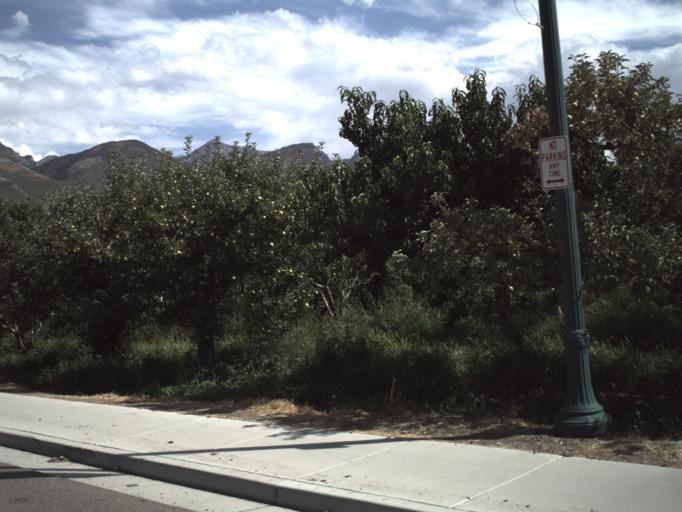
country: US
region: Utah
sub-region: Utah County
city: Orem
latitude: 40.3119
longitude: -111.6767
